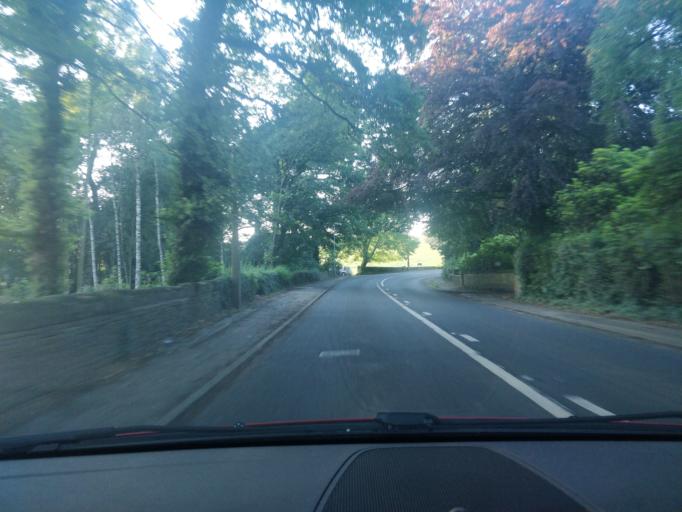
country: GB
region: England
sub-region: Lancashire
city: Parbold
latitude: 53.5990
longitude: -2.7685
